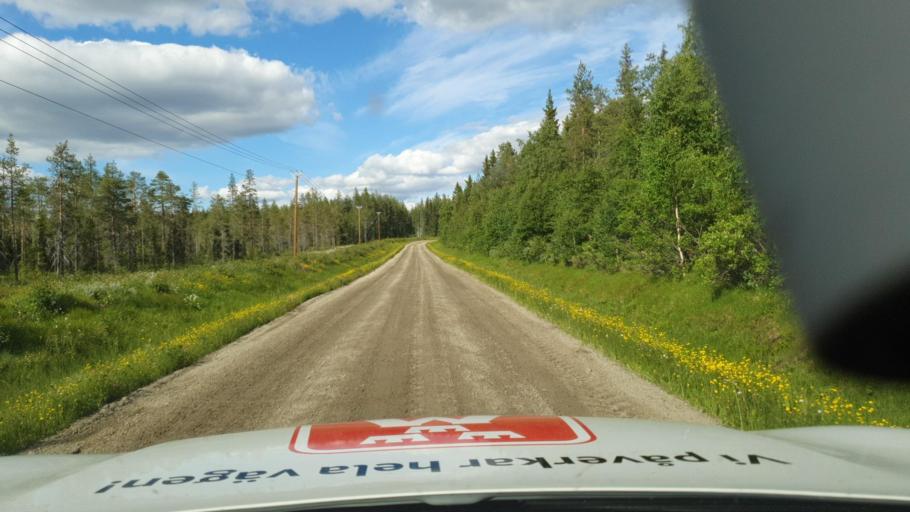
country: SE
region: Vaesterbotten
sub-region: Lycksele Kommun
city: Lycksele
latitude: 64.3262
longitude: 18.3506
